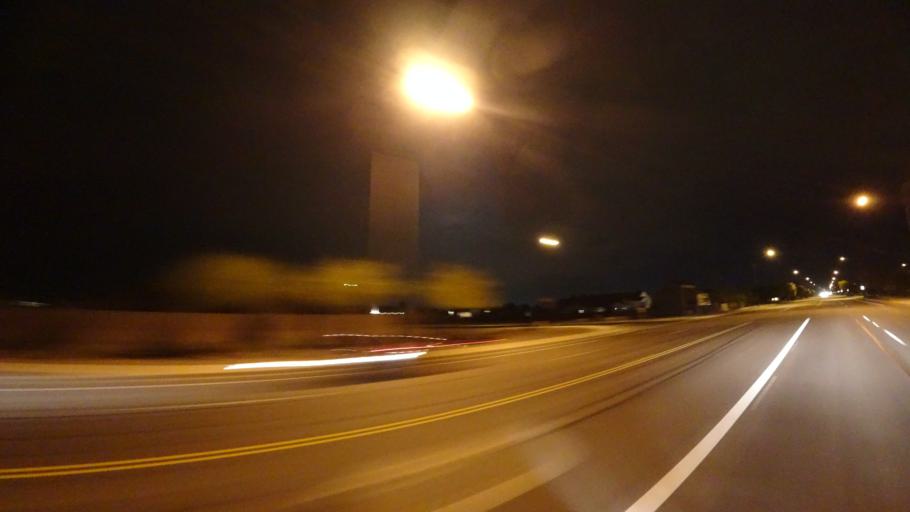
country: US
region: Arizona
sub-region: Maricopa County
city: Queen Creek
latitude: 33.2407
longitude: -111.7381
